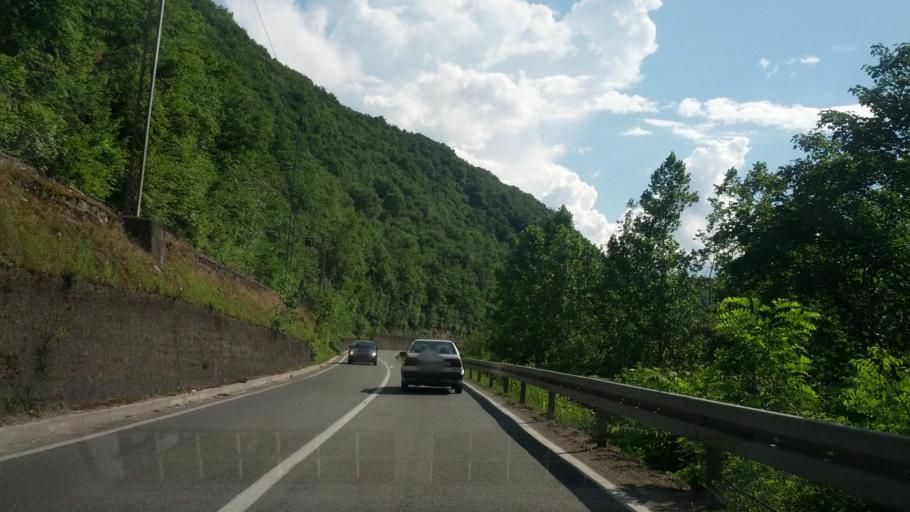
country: BA
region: Federation of Bosnia and Herzegovina
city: Ostrozac
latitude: 44.8912
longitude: 15.9234
